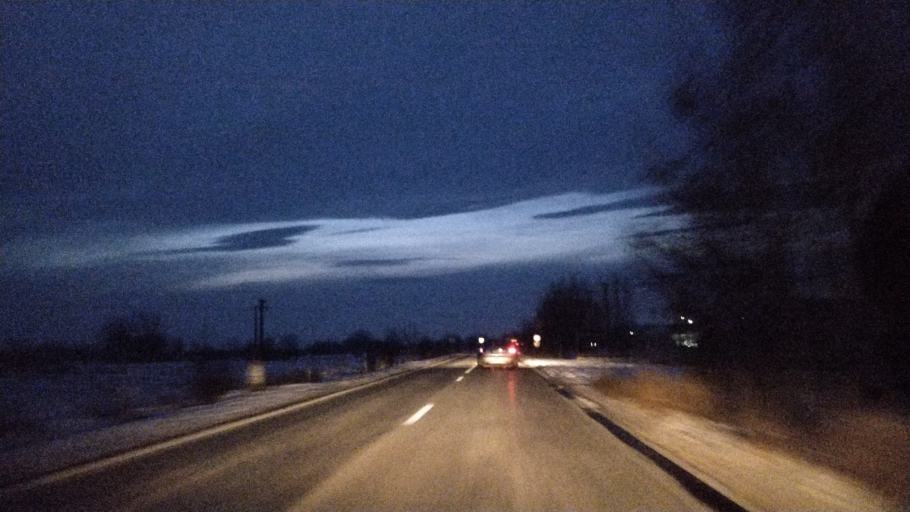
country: RO
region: Vrancea
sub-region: Comuna Milcovul
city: Milcovul
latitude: 45.6776
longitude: 27.2392
